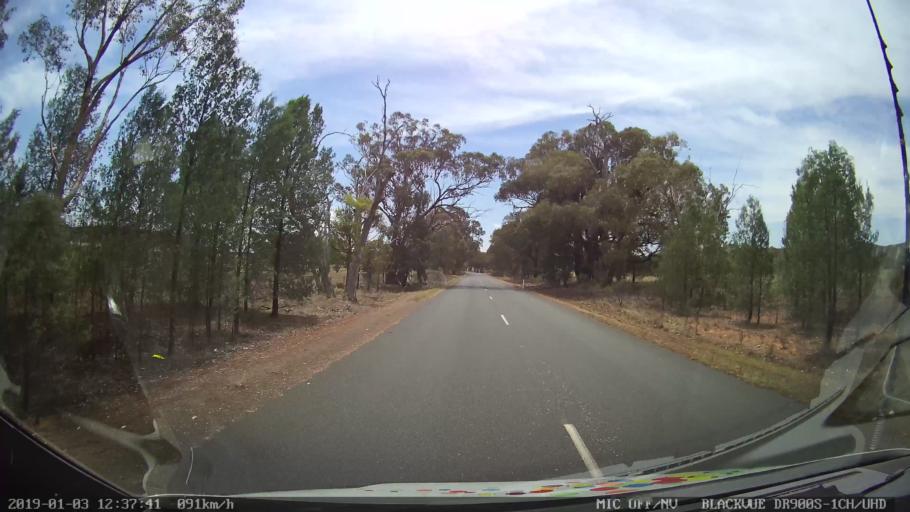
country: AU
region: New South Wales
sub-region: Weddin
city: Grenfell
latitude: -33.8404
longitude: 148.1868
